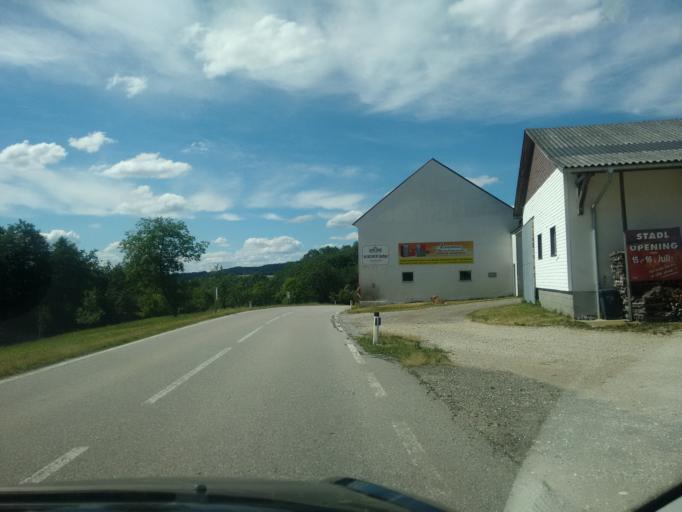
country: AT
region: Upper Austria
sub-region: Politischer Bezirk Ried im Innkreis
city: Ried im Innkreis
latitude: 48.2184
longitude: 13.4115
